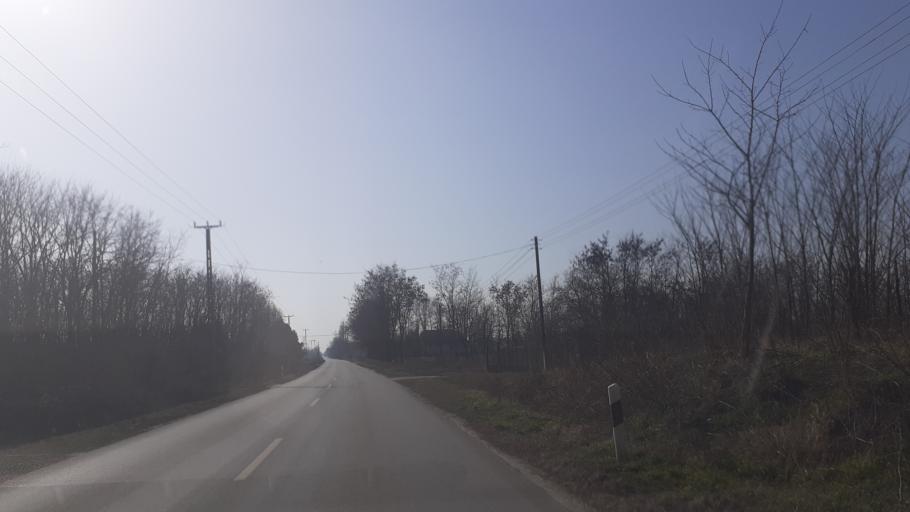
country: HU
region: Bacs-Kiskun
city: Lajosmizse
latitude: 47.0229
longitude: 19.5267
